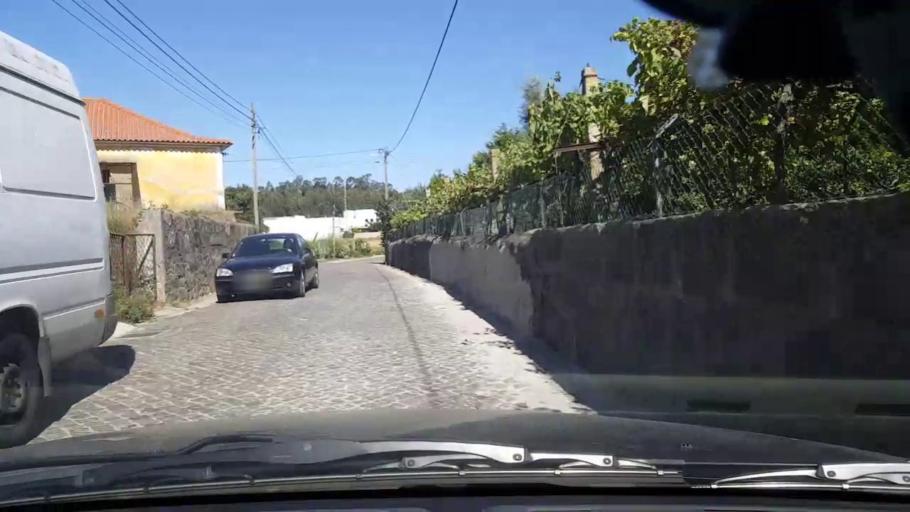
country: PT
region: Porto
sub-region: Maia
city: Gemunde
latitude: 41.2793
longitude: -8.6724
